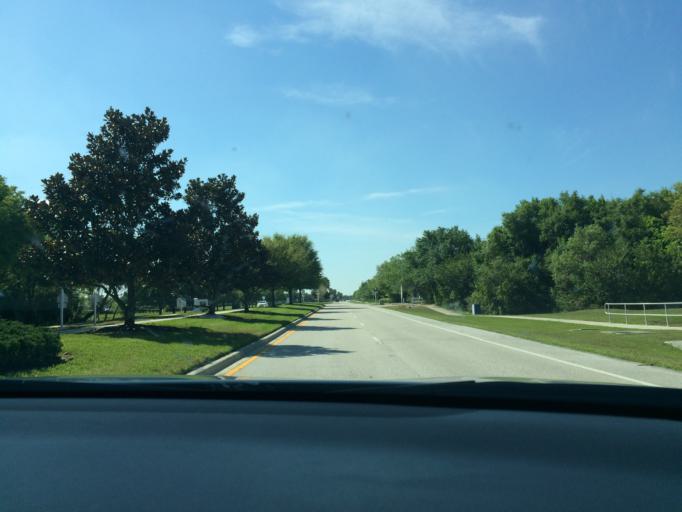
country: US
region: Florida
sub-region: Sarasota County
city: The Meadows
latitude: 27.3950
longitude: -82.3985
